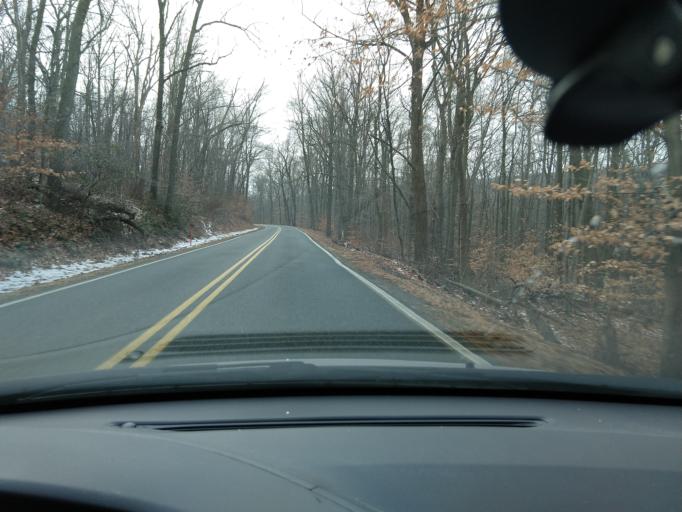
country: US
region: Pennsylvania
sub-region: Berks County
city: Birdsboro
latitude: 40.2290
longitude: -75.7743
